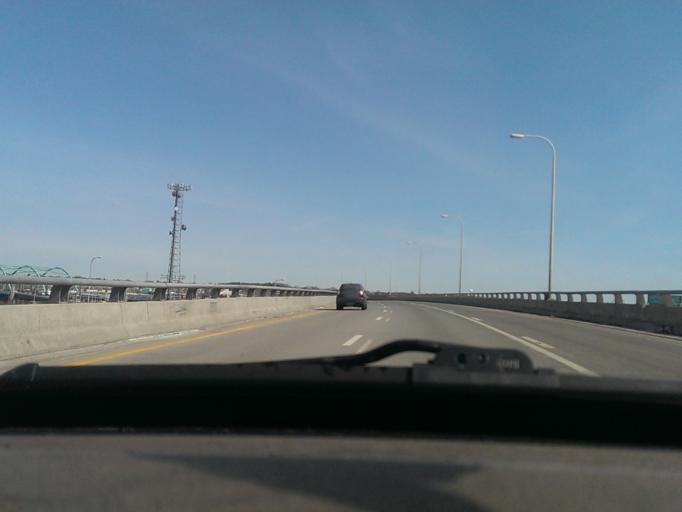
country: US
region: Rhode Island
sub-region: Providence County
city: Providence
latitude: 41.8136
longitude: -71.4091
